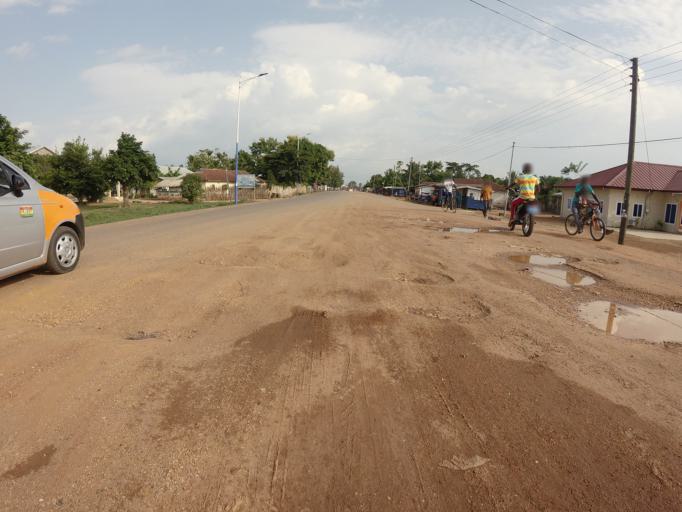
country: GH
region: Volta
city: Hohoe
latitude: 7.1397
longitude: 0.4629
